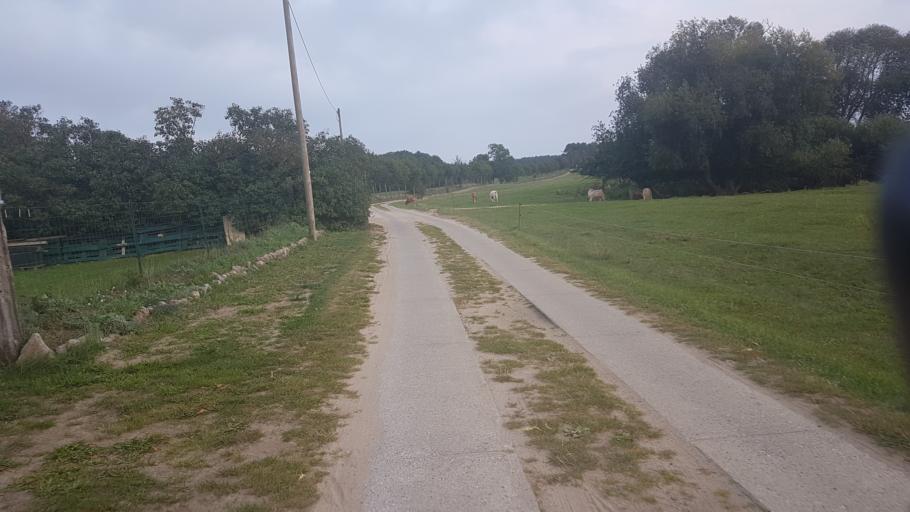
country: DE
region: Mecklenburg-Vorpommern
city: Putbus
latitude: 54.3528
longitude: 13.5247
